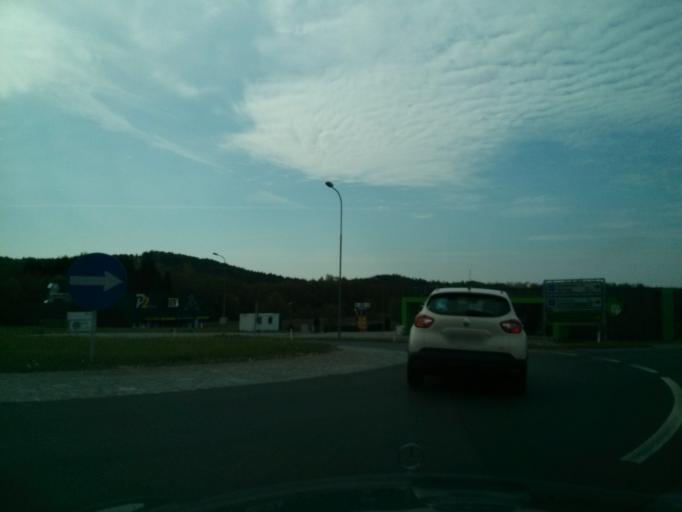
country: AT
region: Burgenland
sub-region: Politischer Bezirk Oberwart
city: Kemeten
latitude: 47.2756
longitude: 16.1570
